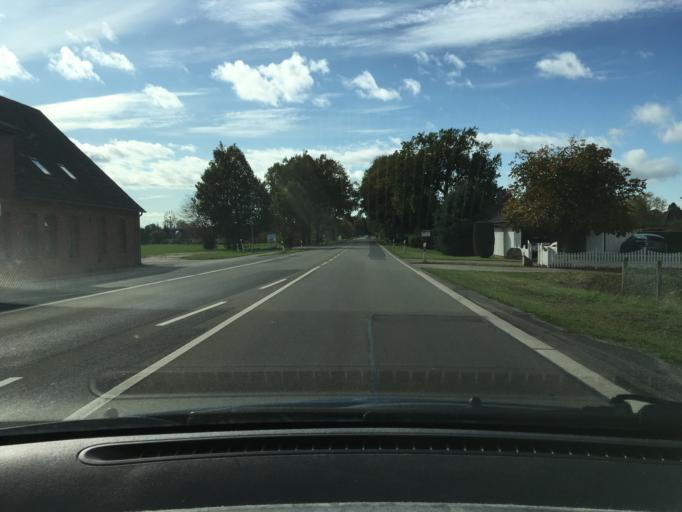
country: DE
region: Lower Saxony
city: Wistedt
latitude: 53.2701
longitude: 9.6809
